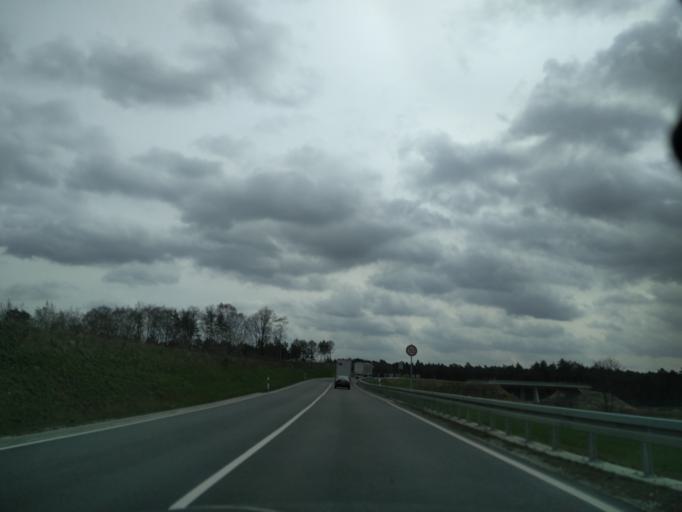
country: DE
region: North Rhine-Westphalia
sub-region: Regierungsbezirk Detmold
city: Steinhagen
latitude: 52.0245
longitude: 8.3827
